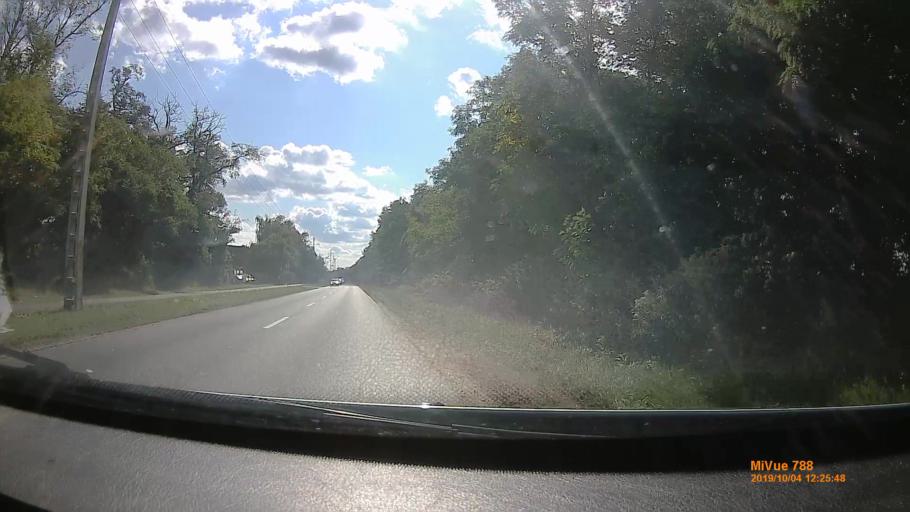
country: HU
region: Szabolcs-Szatmar-Bereg
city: Nyiregyhaza
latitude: 47.9823
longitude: 21.7046
